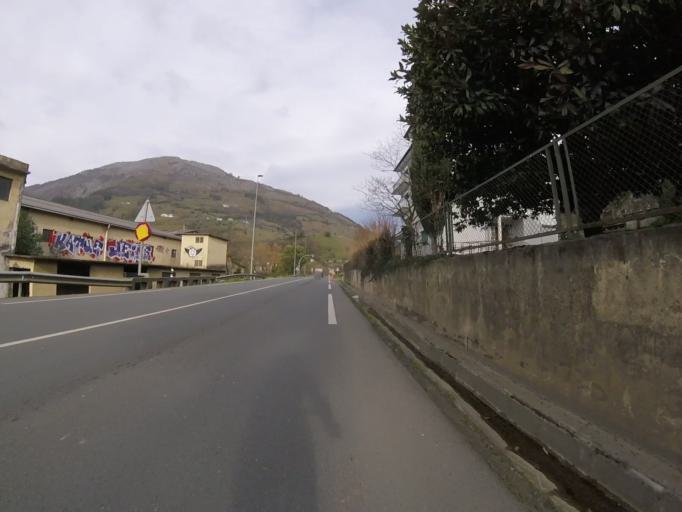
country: ES
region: Basque Country
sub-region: Provincia de Guipuzcoa
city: Azpeitia
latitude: 43.1849
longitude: -2.2603
